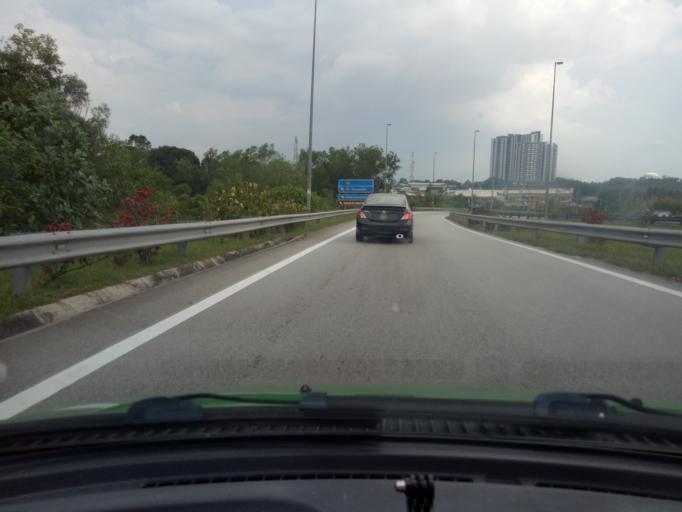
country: MY
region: Selangor
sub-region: Hulu Langat
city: Semenyih
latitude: 2.9712
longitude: 101.8349
